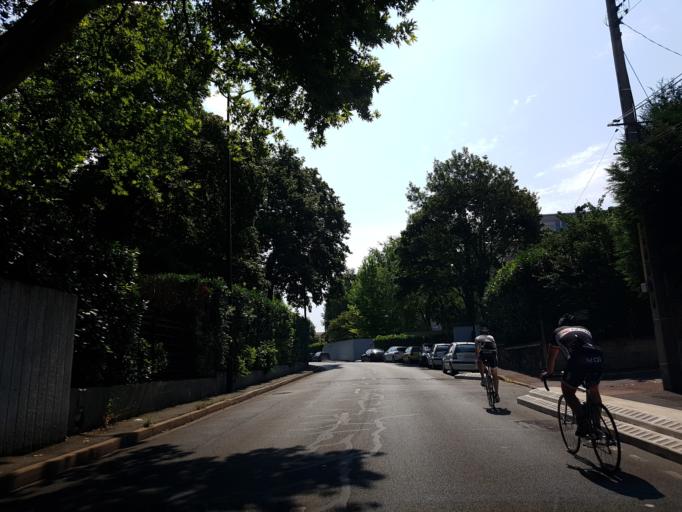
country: FR
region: Ile-de-France
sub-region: Departement du Val-de-Marne
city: L'Hay-les-Roses
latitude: 48.7739
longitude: 2.3336
